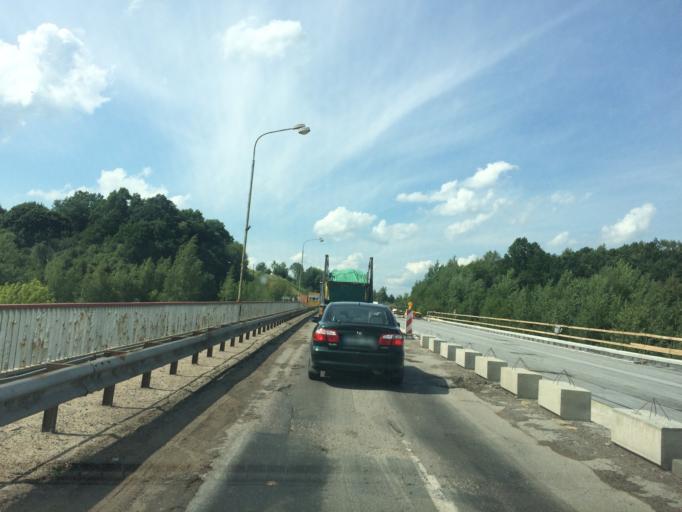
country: LT
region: Kauno apskritis
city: Jonava
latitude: 55.0879
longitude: 24.3150
